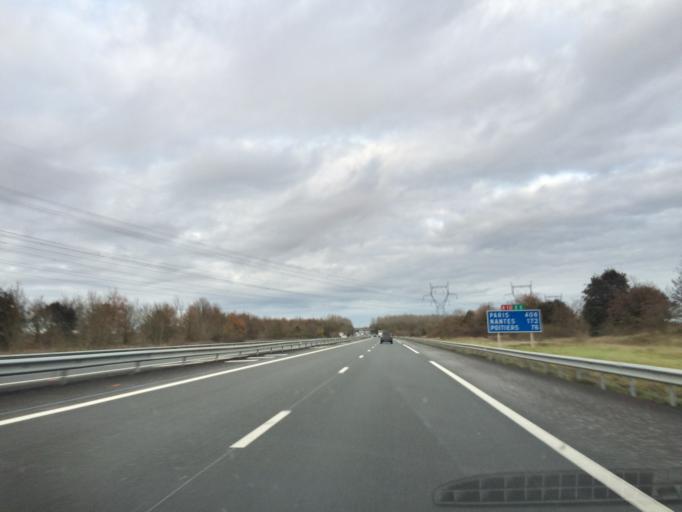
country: FR
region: Poitou-Charentes
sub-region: Departement des Deux-Sevres
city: Fors
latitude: 46.2484
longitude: -0.4267
